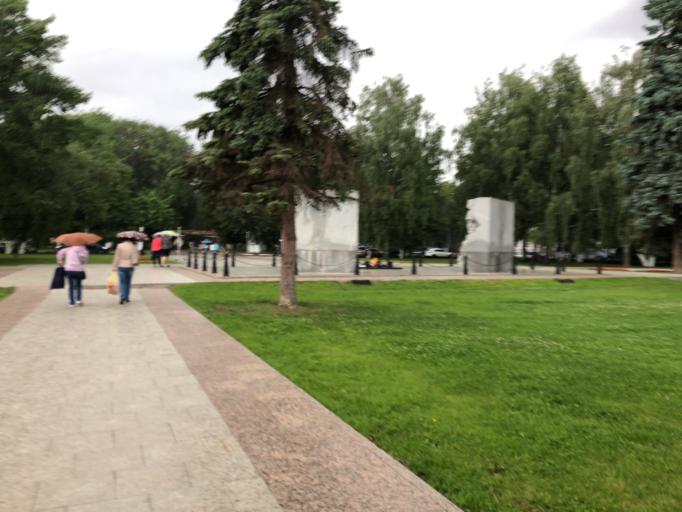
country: RU
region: Jaroslavl
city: Yaroslavl
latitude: 57.6236
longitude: 39.8994
